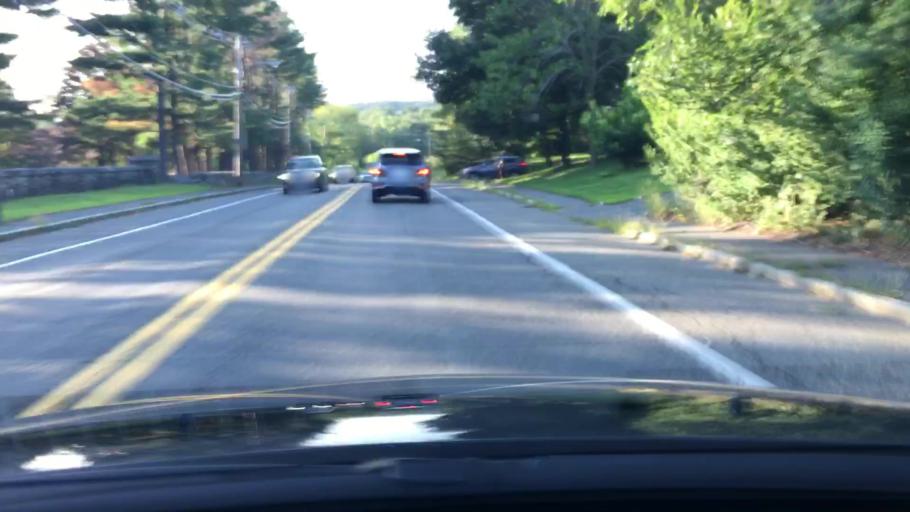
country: US
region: Massachusetts
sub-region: Worcester County
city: Shrewsbury
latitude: 42.3002
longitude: -71.7147
